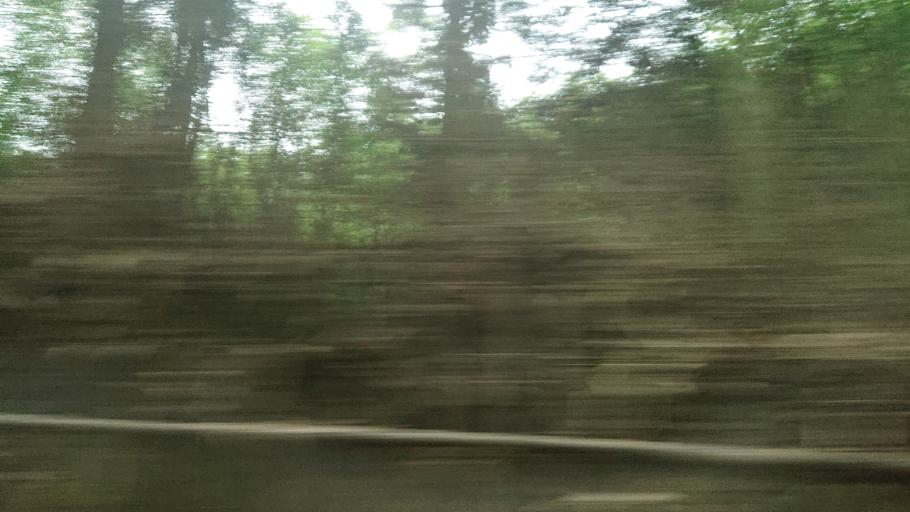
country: TW
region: Taiwan
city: Lugu
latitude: 23.6240
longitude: 120.7135
